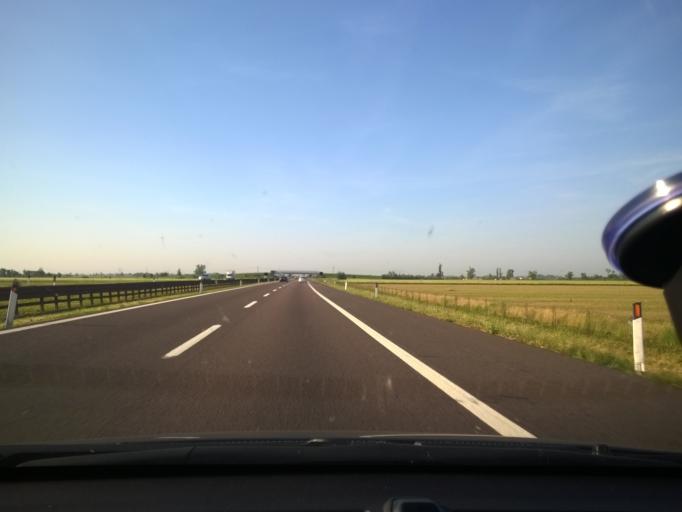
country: IT
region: Emilia-Romagna
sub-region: Provincia di Reggio Emilia
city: Rolo
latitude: 44.8611
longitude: 10.8514
